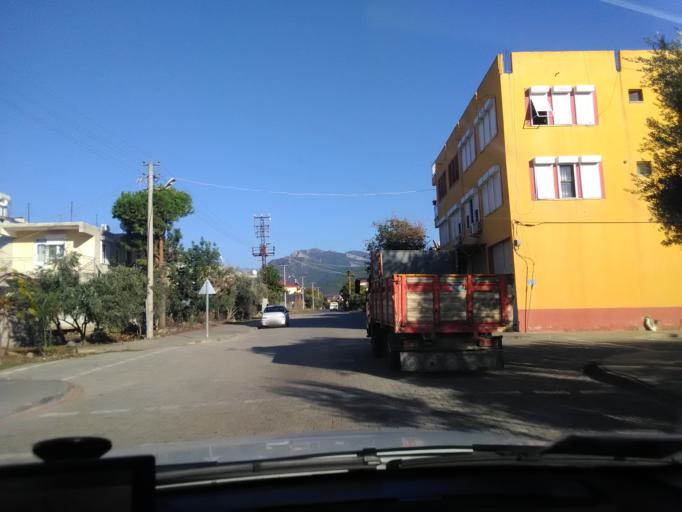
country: TR
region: Antalya
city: Gazipasa
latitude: 36.2703
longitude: 32.3279
